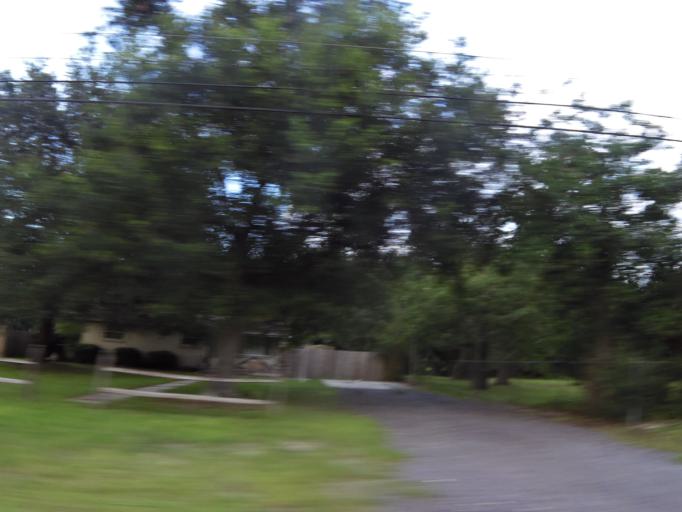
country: US
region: Florida
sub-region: Duval County
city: Jacksonville
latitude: 30.3548
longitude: -81.8069
